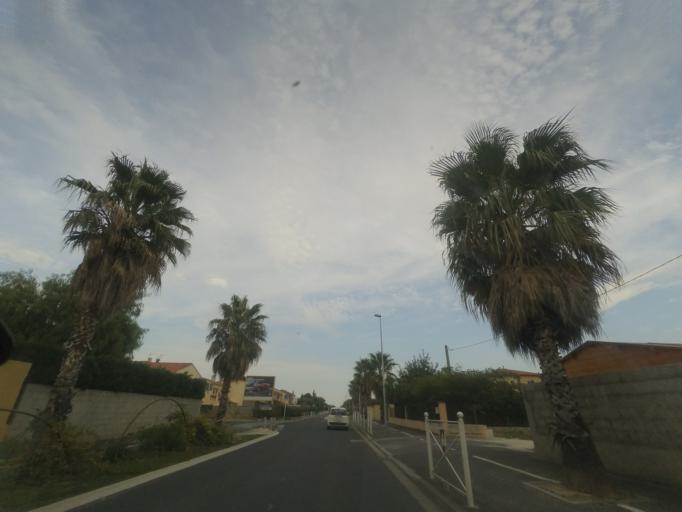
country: FR
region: Languedoc-Roussillon
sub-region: Departement des Pyrenees-Orientales
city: Le Soler
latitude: 42.6832
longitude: 2.8027
